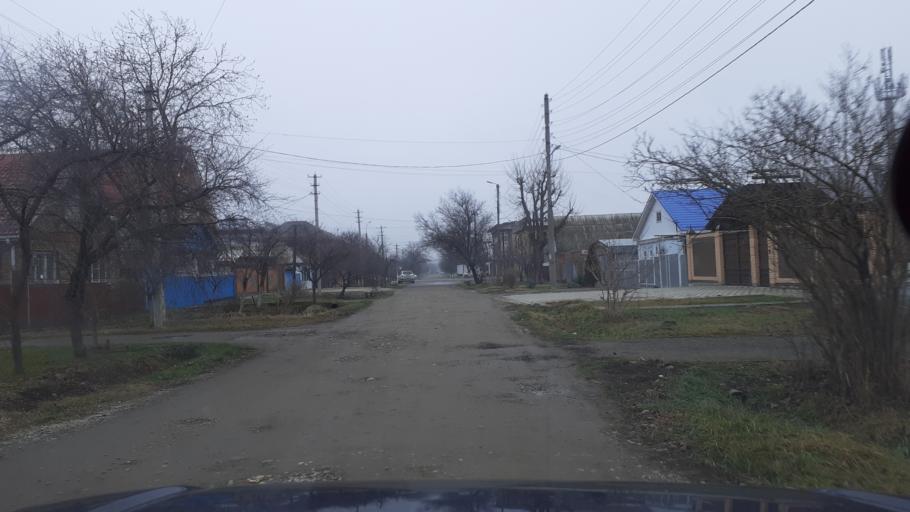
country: RU
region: Adygeya
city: Maykop
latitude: 44.6183
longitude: 40.0880
